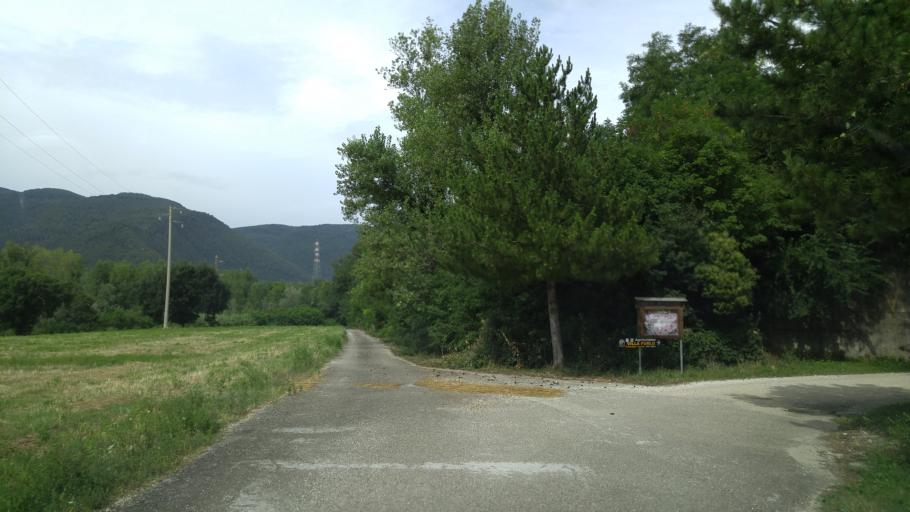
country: IT
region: The Marches
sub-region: Provincia di Pesaro e Urbino
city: Fossombrone
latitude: 43.6678
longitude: 12.7583
